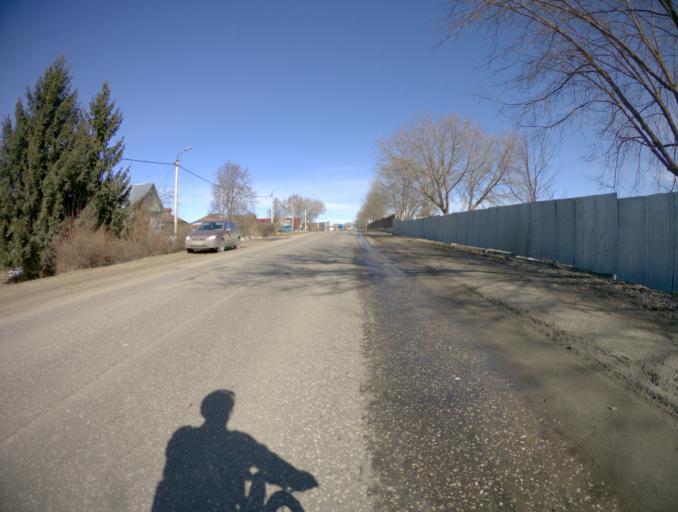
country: RU
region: Vladimir
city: Suzdal'
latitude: 56.4327
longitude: 40.4240
